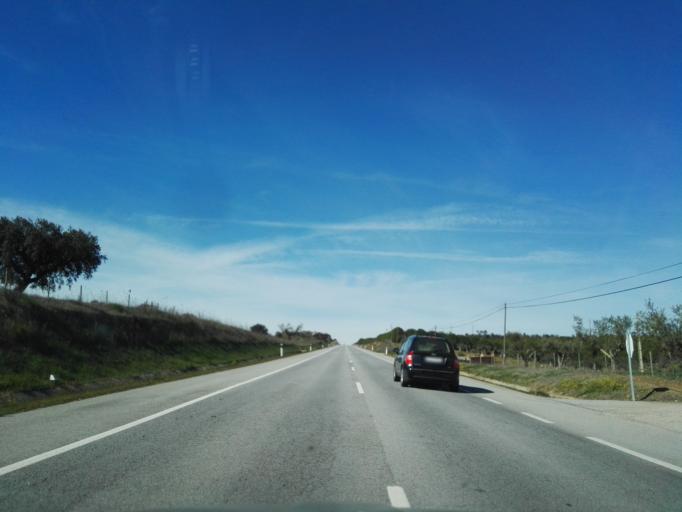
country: PT
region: Portalegre
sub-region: Arronches
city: Arronches
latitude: 39.1439
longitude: -7.3022
